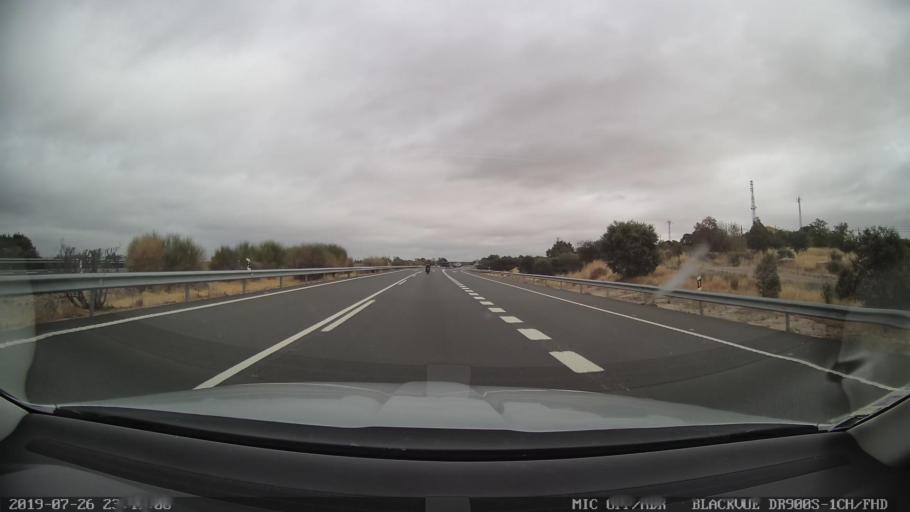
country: ES
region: Extremadura
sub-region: Provincia de Caceres
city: Trujillo
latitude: 39.4794
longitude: -5.8516
